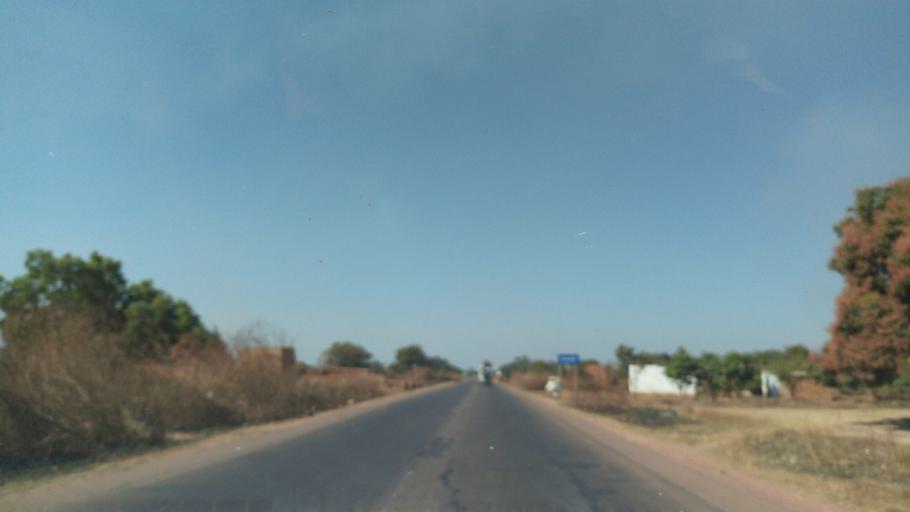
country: CD
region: Katanga
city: Lubumbashi
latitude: -11.5612
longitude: 27.5682
